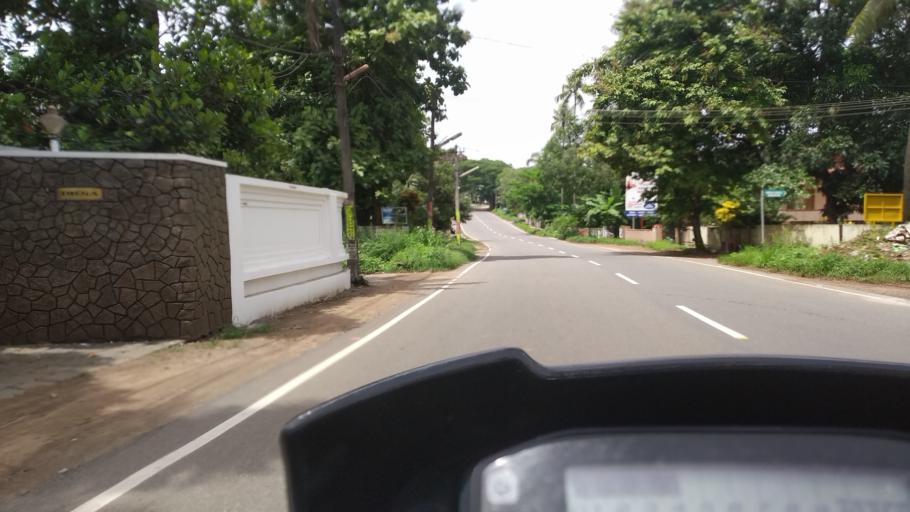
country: IN
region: Kerala
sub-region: Ernakulam
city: Aluva
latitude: 10.1263
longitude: 76.3218
